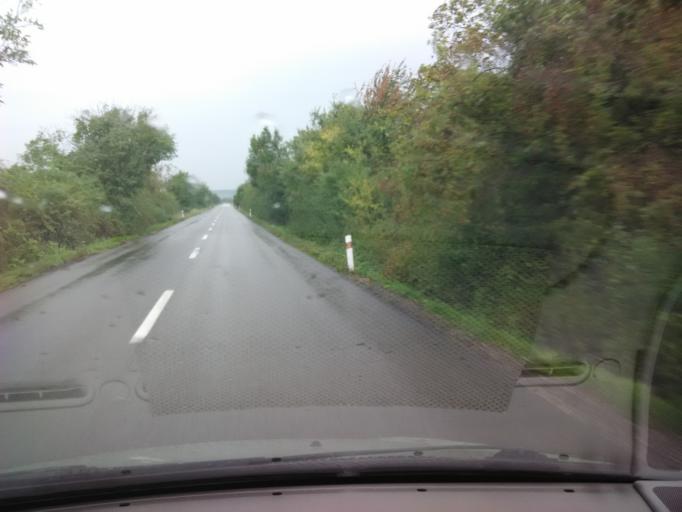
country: SK
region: Nitriansky
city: Tlmace
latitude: 48.3363
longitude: 18.4902
